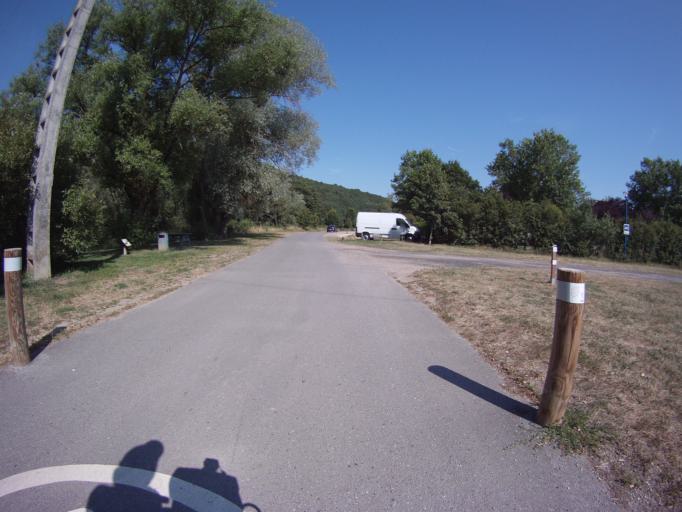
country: FR
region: Lorraine
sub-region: Departement de Meurthe-et-Moselle
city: Liverdun
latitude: 48.7464
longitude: 6.0577
